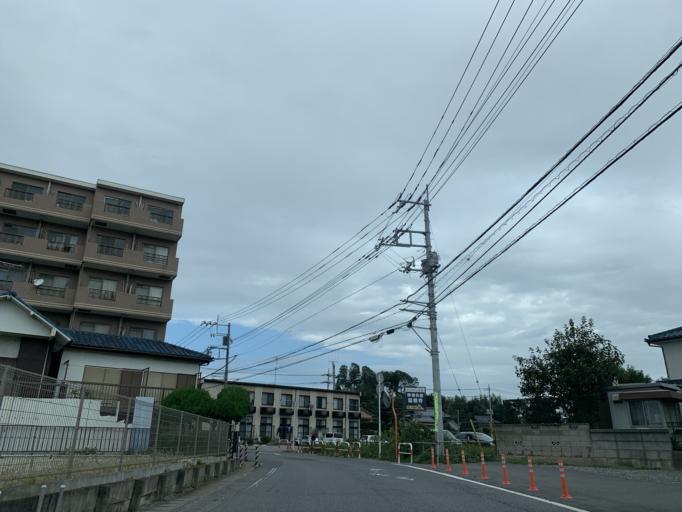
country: JP
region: Chiba
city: Kashiwa
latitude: 35.8753
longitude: 139.9512
